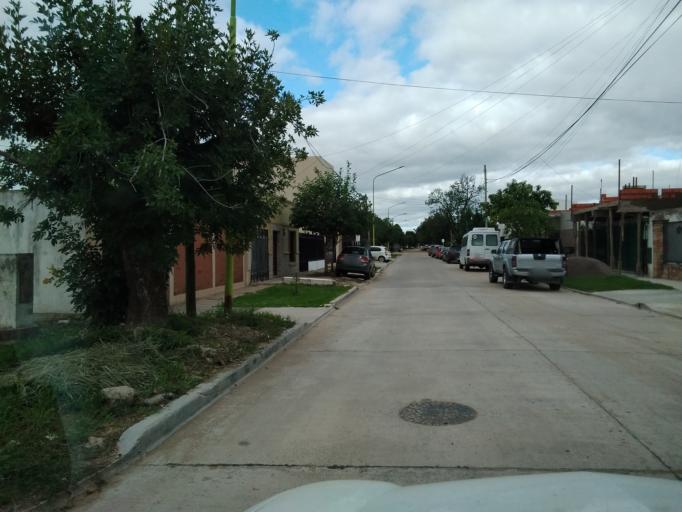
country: AR
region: Corrientes
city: Corrientes
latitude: -27.4736
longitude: -58.8120
